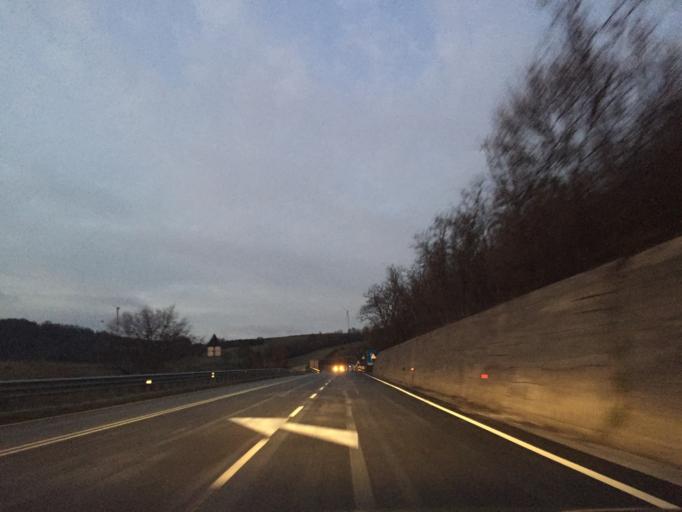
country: IT
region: Apulia
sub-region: Provincia di Foggia
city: Volturino
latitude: 41.4646
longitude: 15.0940
